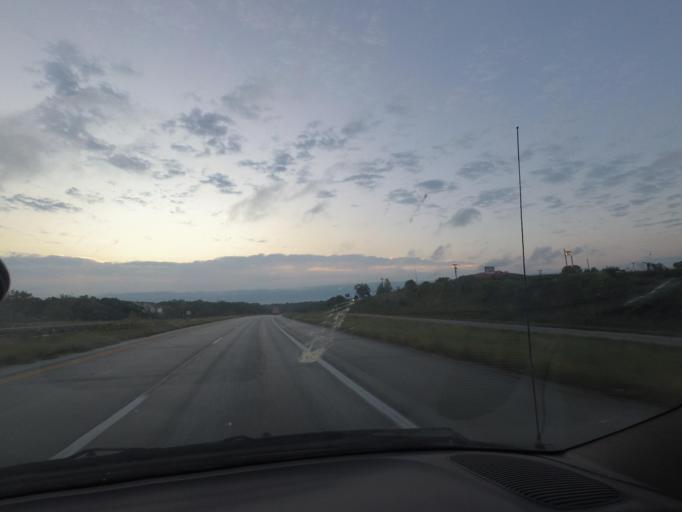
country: US
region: Missouri
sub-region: Macon County
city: Macon
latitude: 39.7485
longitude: -92.5042
